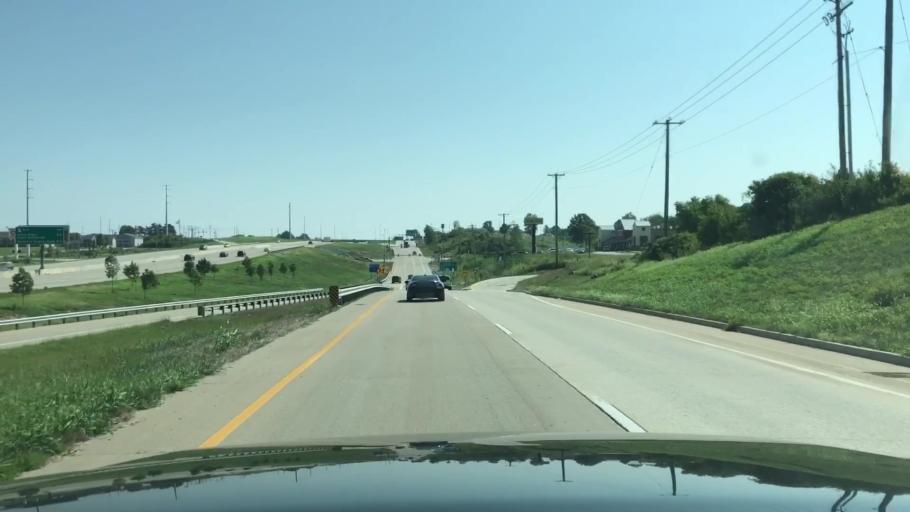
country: US
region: Missouri
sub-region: Saint Charles County
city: Saint Peters
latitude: 38.7471
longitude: -90.5882
